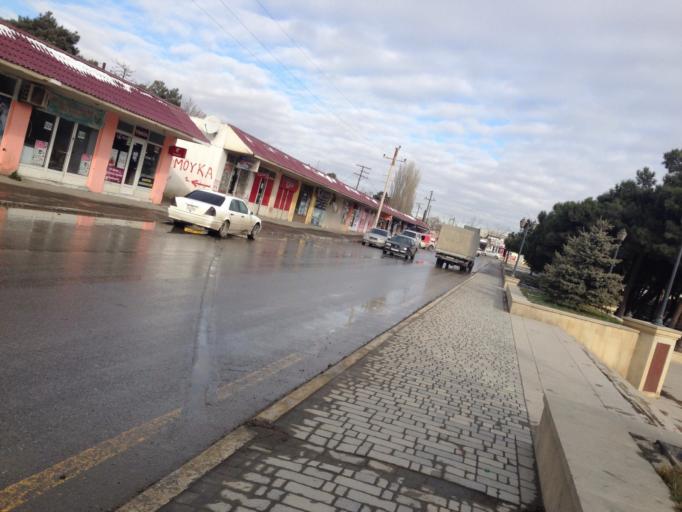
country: AZ
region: Baki
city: Baku
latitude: 40.3975
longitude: 49.8929
